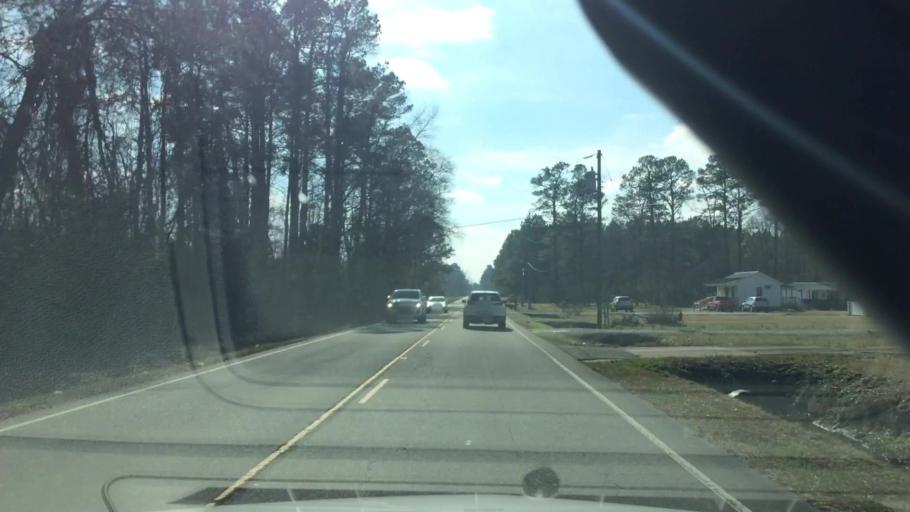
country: US
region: North Carolina
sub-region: Duplin County
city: Beulaville
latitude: 34.8683
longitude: -77.7926
